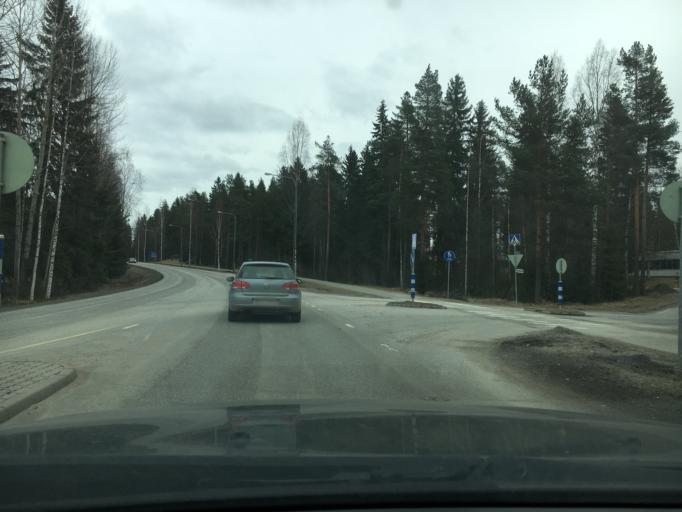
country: FI
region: Central Finland
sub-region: AEaenekoski
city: Suolahti
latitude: 62.5594
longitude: 25.8626
